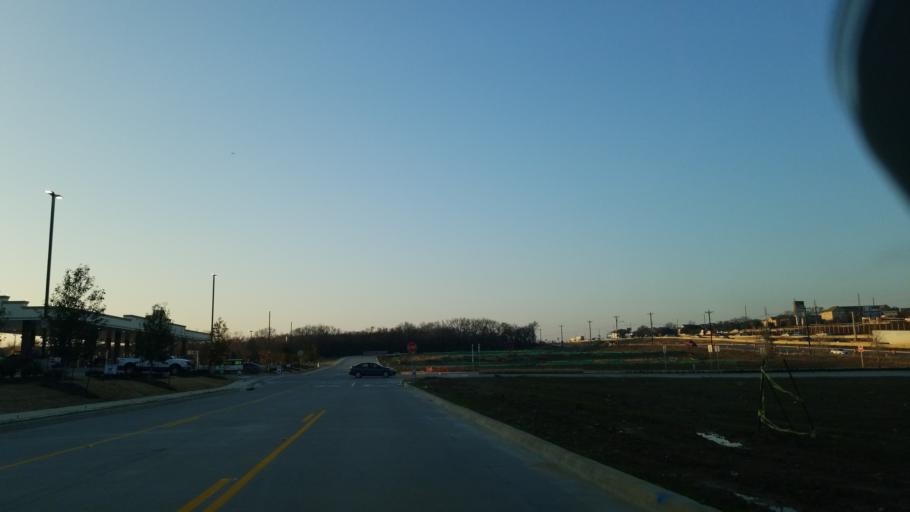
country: US
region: Texas
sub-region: Denton County
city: Corinth
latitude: 33.1797
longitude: -97.1013
